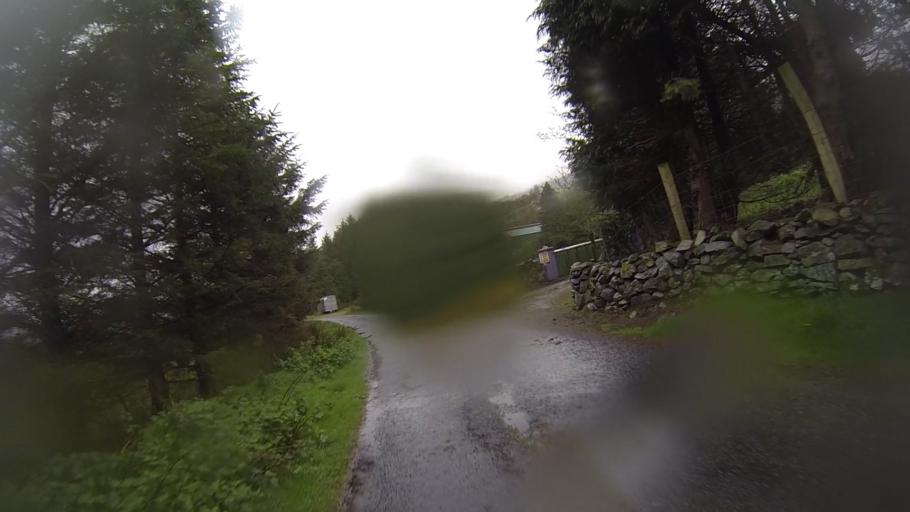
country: IE
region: Munster
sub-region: Ciarrai
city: Kenmare
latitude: 51.9489
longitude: -9.6704
